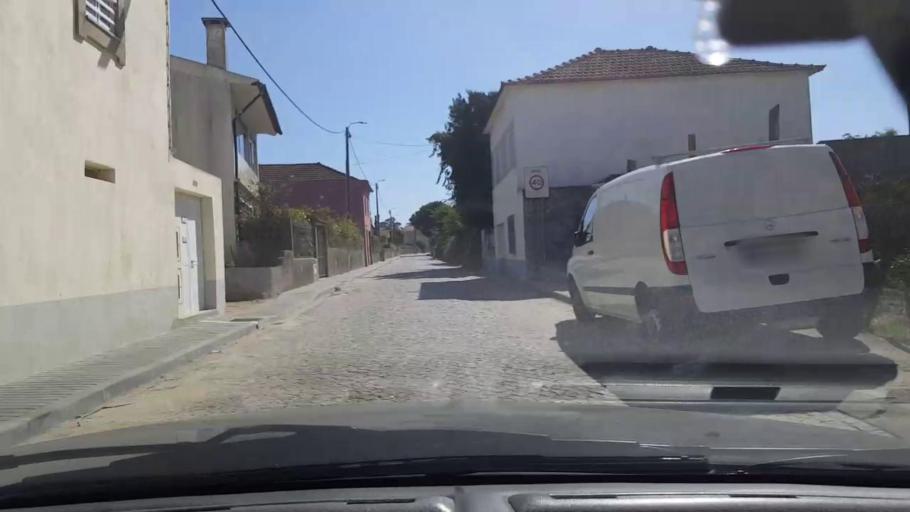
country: PT
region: Porto
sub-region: Vila do Conde
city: Arvore
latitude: 41.3108
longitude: -8.7188
